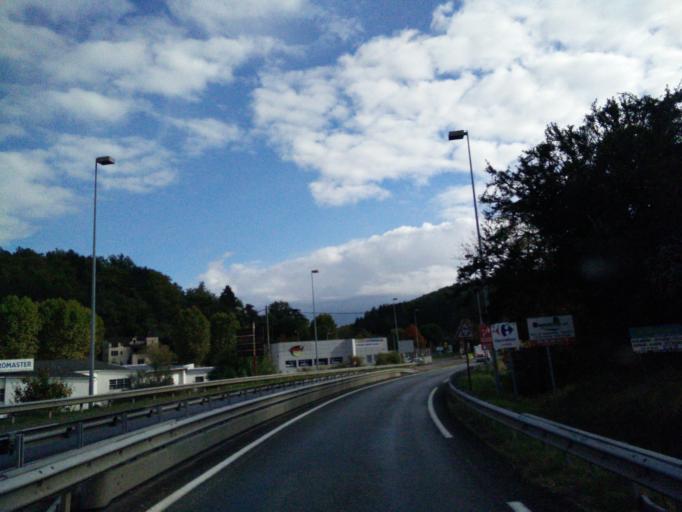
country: FR
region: Midi-Pyrenees
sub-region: Departement du Lot
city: Cahors
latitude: 44.4276
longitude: 1.4405
